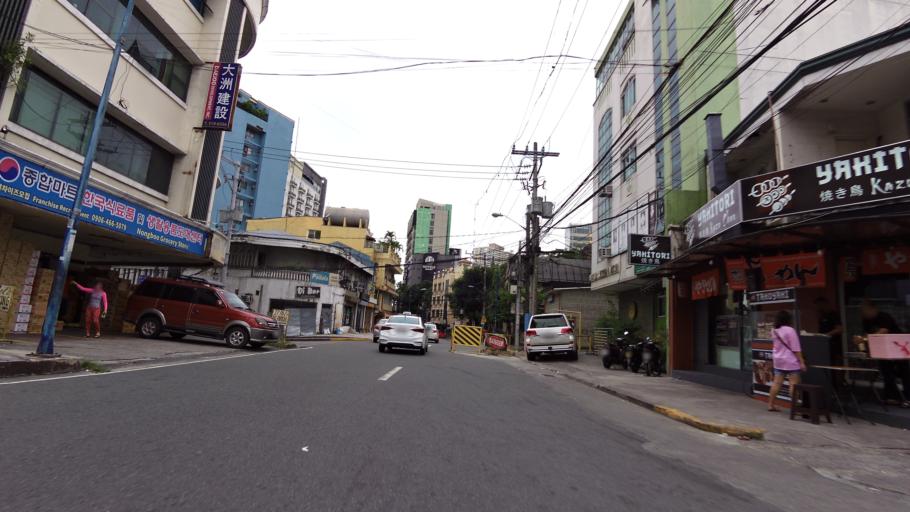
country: PH
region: Metro Manila
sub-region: Makati City
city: Makati City
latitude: 14.5653
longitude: 121.0311
